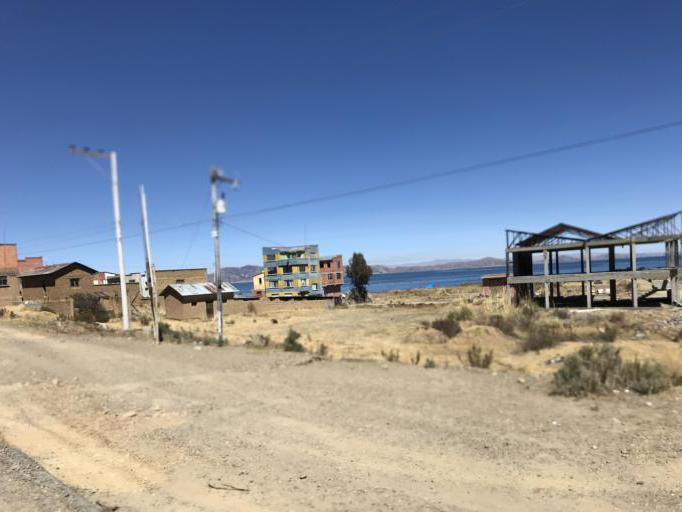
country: BO
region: La Paz
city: Huatajata
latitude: -16.2107
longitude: -68.6922
